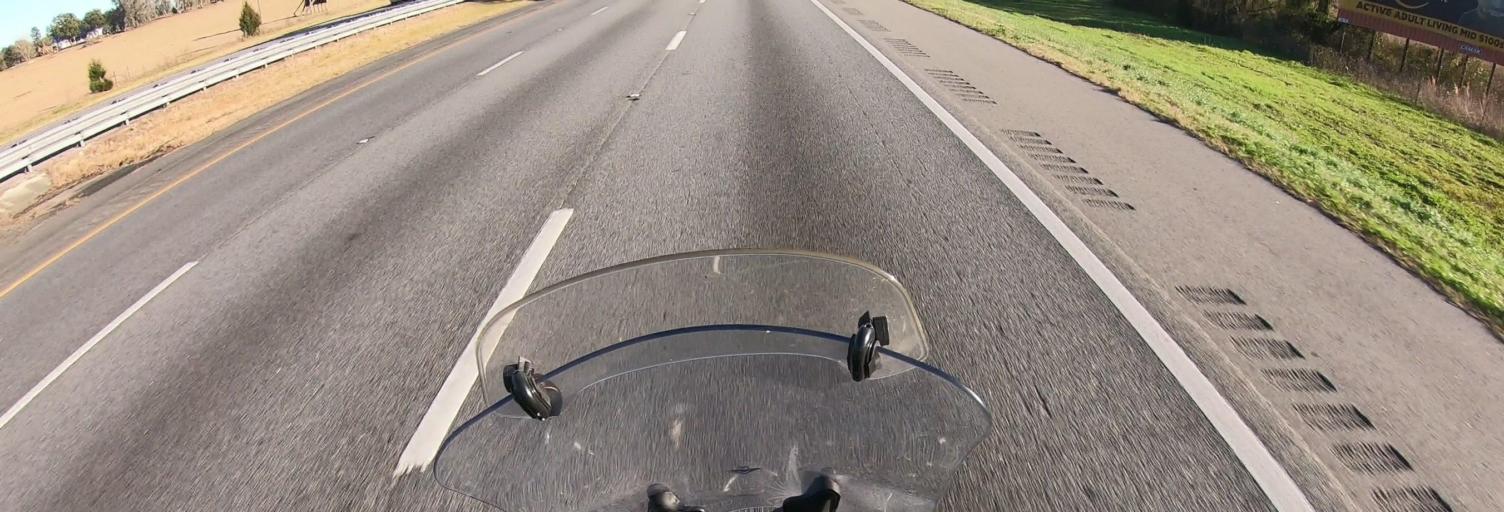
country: US
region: Florida
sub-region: Alachua County
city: Alachua
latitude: 29.7592
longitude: -82.5016
